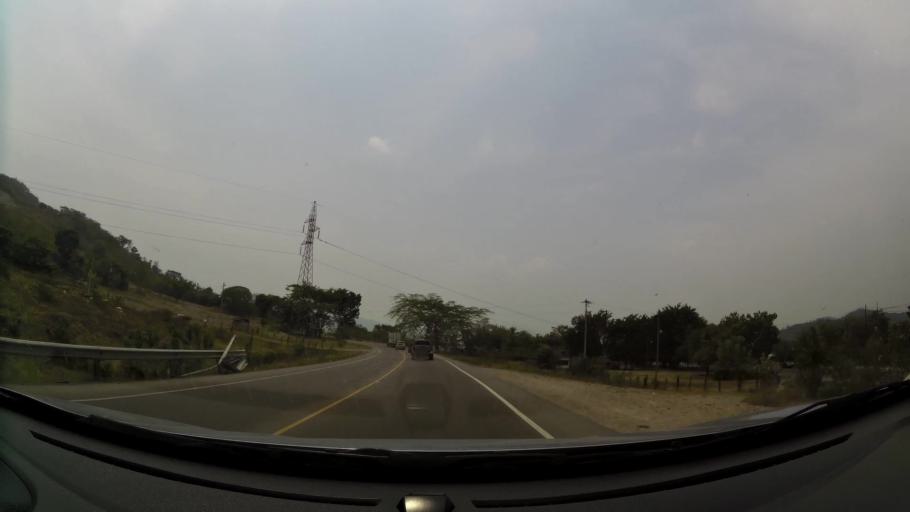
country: HN
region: Cortes
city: El Plan
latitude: 15.2630
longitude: -87.9618
